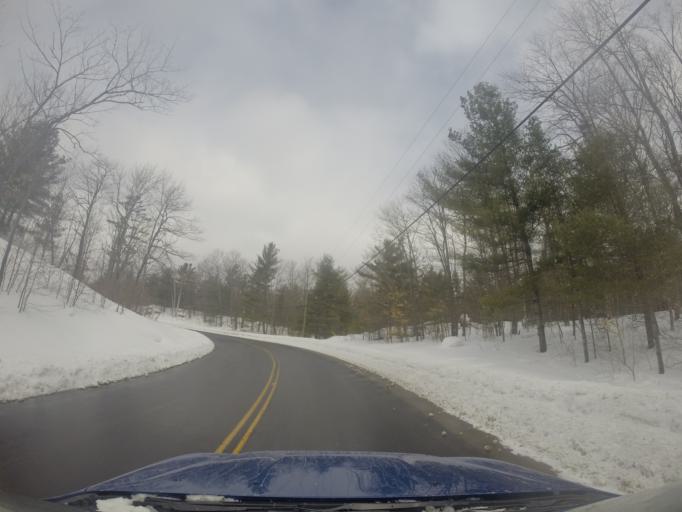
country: CA
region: Ontario
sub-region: Parry Sound District
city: Parry Sound
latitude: 45.3773
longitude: -80.0243
